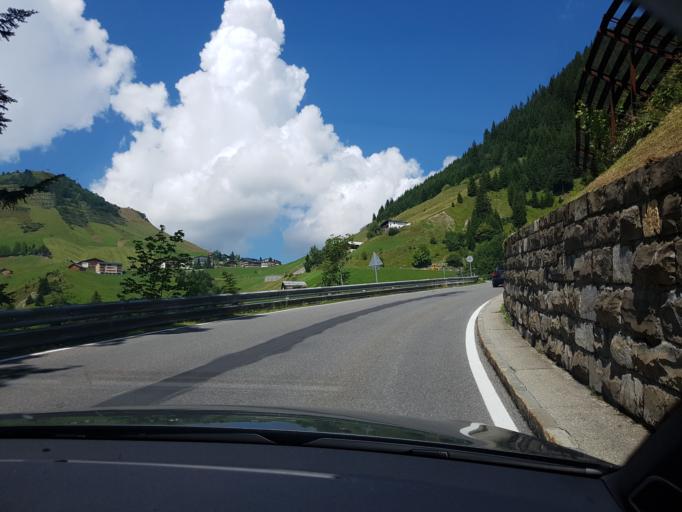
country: AT
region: Vorarlberg
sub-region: Politischer Bezirk Bregenz
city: Damuels
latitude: 47.2634
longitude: 9.9112
